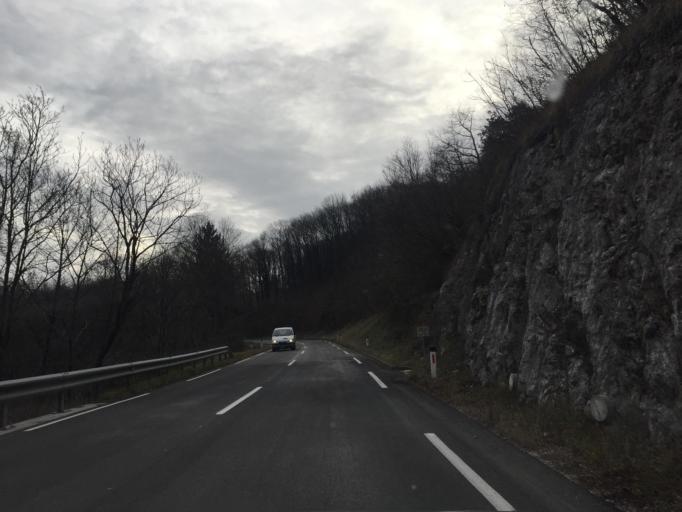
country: SI
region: Nova Gorica
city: Kromberk
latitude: 45.9819
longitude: 13.6818
